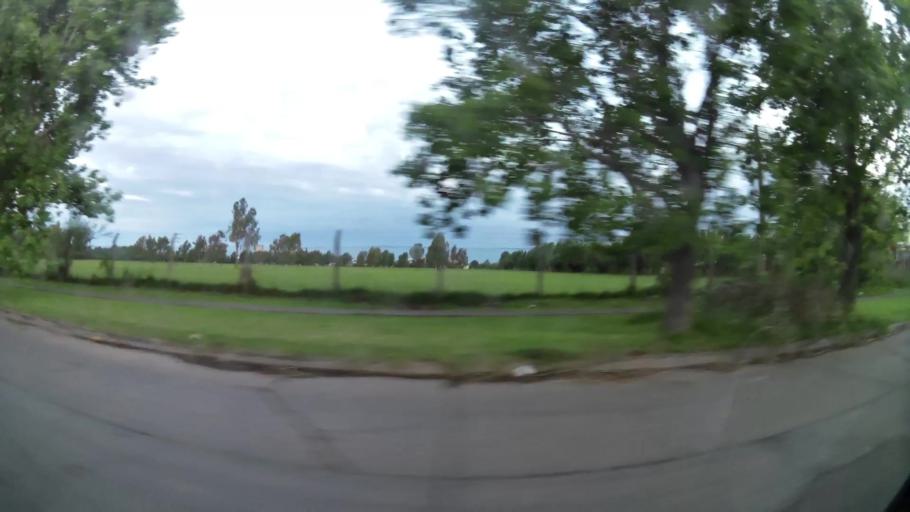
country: AR
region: Buenos Aires
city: San Nicolas de los Arroyos
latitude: -33.3485
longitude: -60.1948
